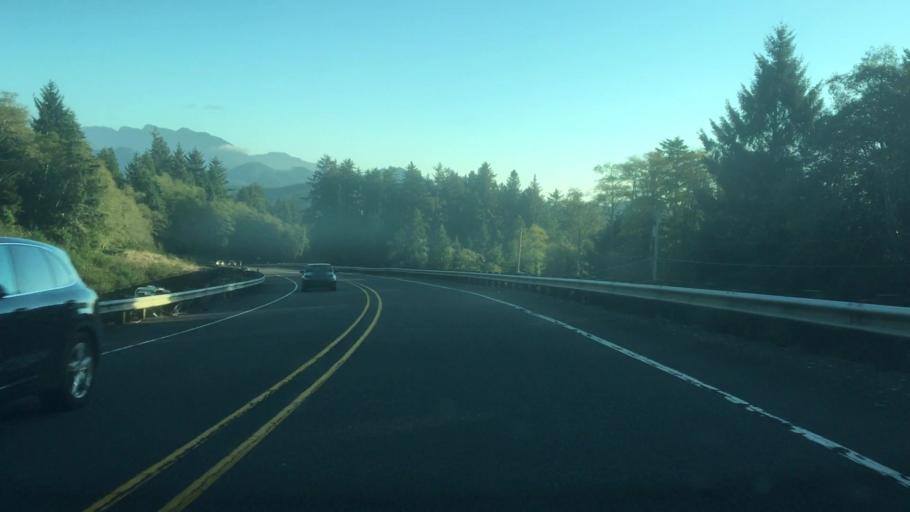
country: US
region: Oregon
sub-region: Clatsop County
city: Cannon Beach
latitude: 45.9054
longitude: -123.9541
